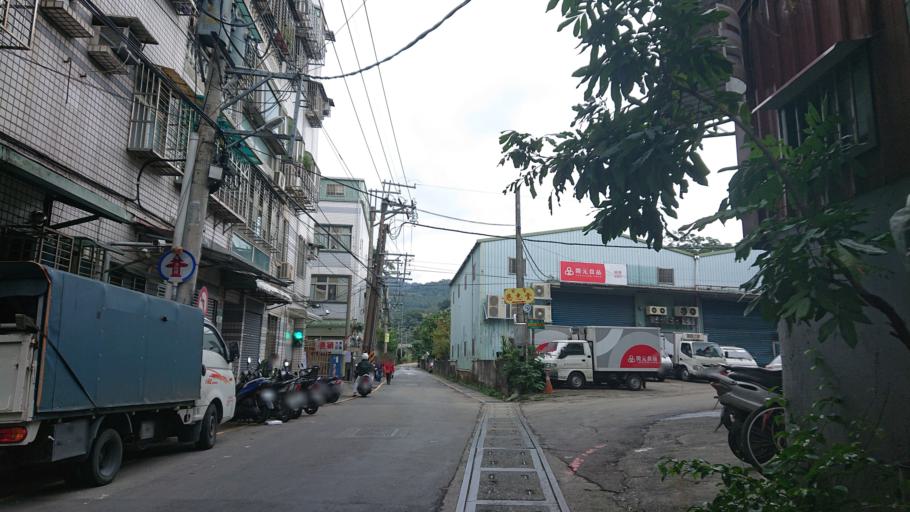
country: TW
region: Taipei
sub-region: Taipei
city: Banqiao
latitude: 24.9626
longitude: 121.4408
